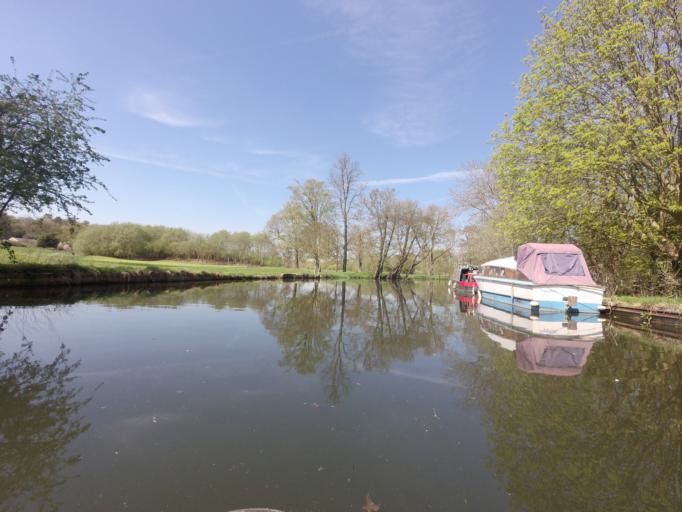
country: GB
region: England
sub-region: Hertfordshire
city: Abbots Langley
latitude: 51.6786
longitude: -0.4310
